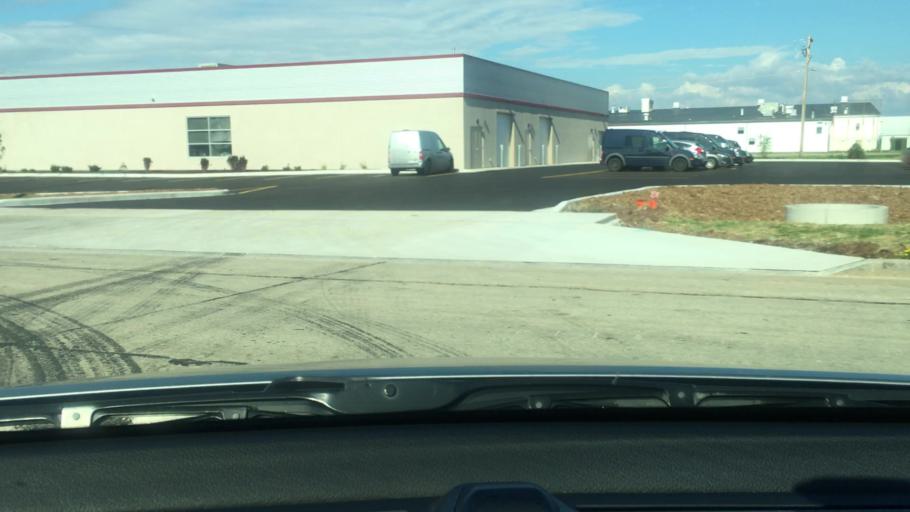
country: US
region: Wisconsin
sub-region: Winnebago County
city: Oshkosh
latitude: 43.9804
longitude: -88.5507
